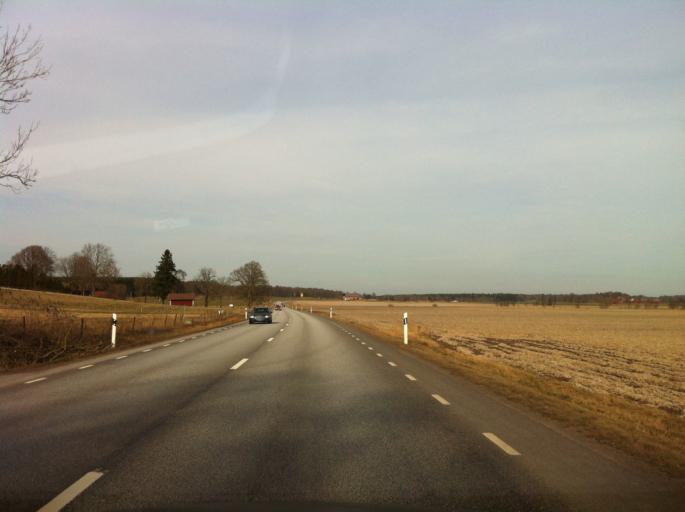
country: SE
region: Vaestra Goetaland
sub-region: Mariestads Kommun
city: Mariestad
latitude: 58.7552
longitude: 13.9454
